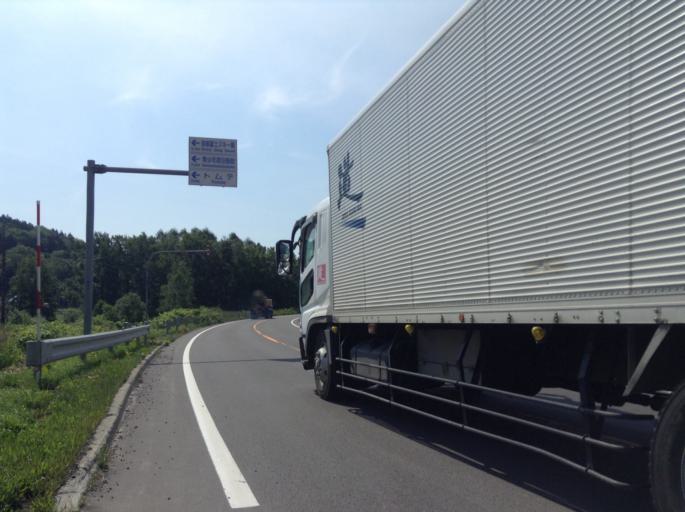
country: JP
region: Hokkaido
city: Nayoro
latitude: 44.7230
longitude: 142.2689
